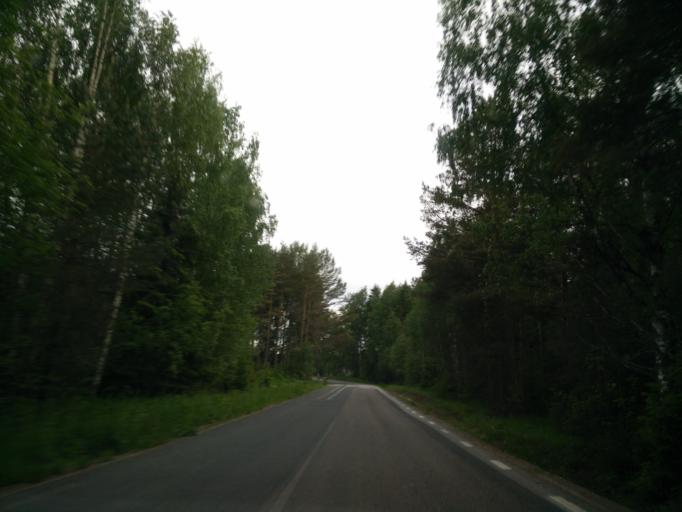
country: SE
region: Vaesternorrland
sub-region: Kramfors Kommun
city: Kramfors
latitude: 63.0356
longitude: 17.7921
